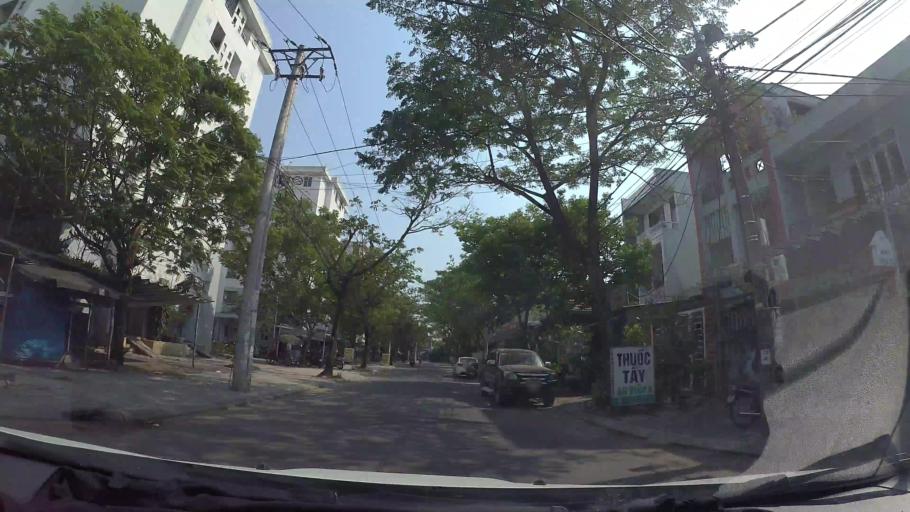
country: VN
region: Da Nang
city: Cam Le
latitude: 16.0072
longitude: 108.1949
